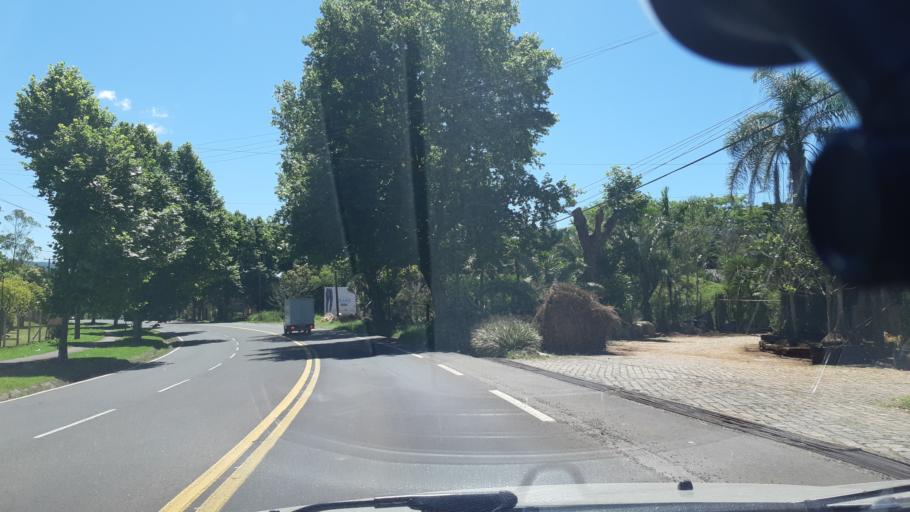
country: BR
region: Rio Grande do Sul
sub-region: Ivoti
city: Ivoti
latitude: -29.6201
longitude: -51.1234
